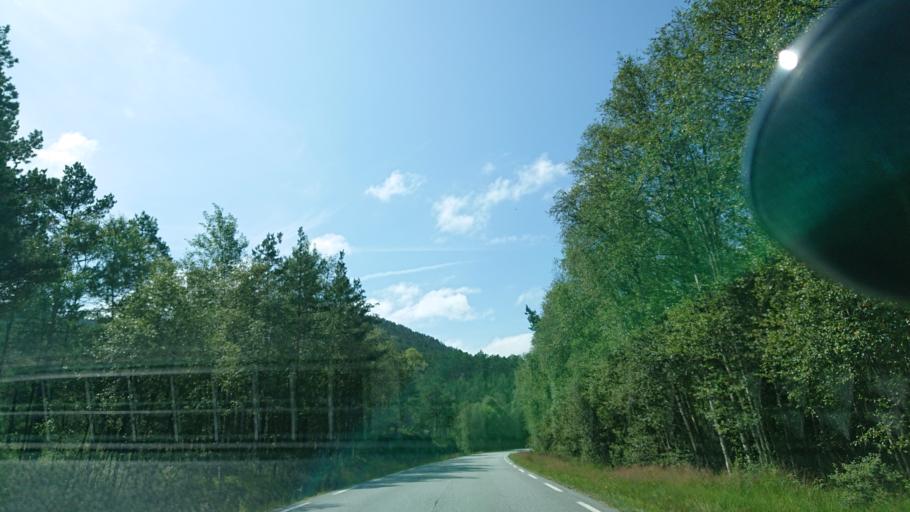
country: NO
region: Rogaland
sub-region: Hjelmeland
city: Hjelmelandsvagen
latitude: 59.2363
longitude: 6.2726
